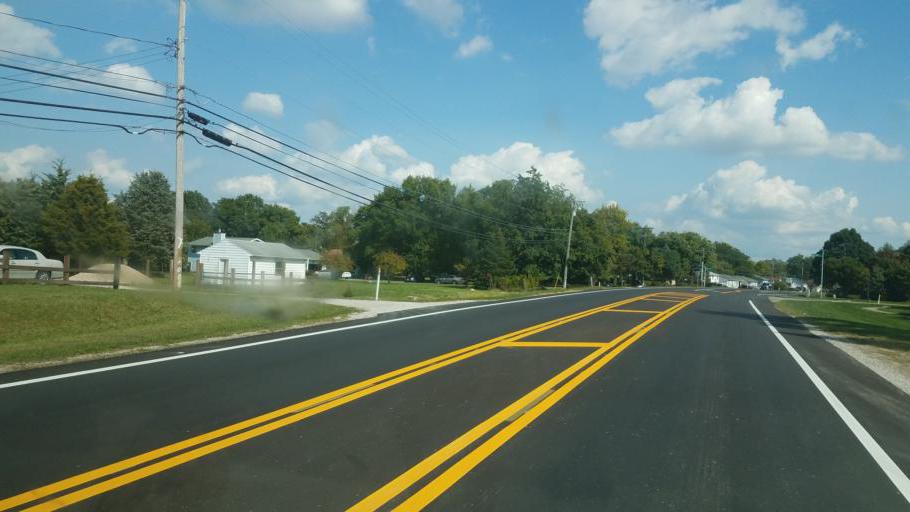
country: US
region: Ohio
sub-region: Franklin County
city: Grove City
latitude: 39.9166
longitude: -83.0945
